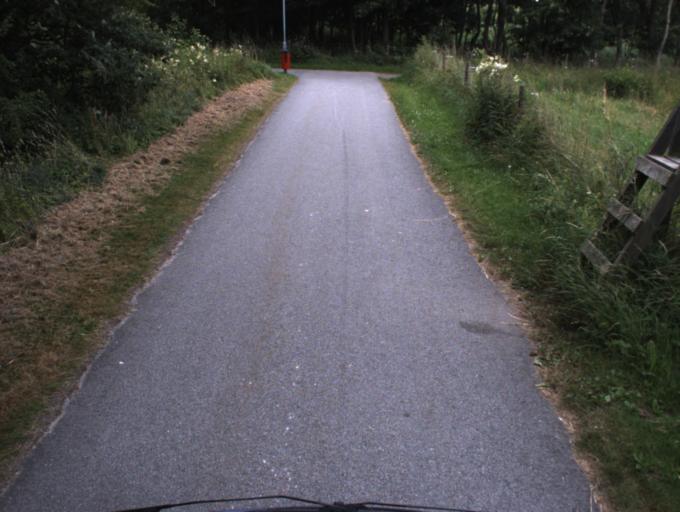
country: SE
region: Skane
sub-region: Helsingborg
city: Rydeback
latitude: 55.9663
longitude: 12.7621
